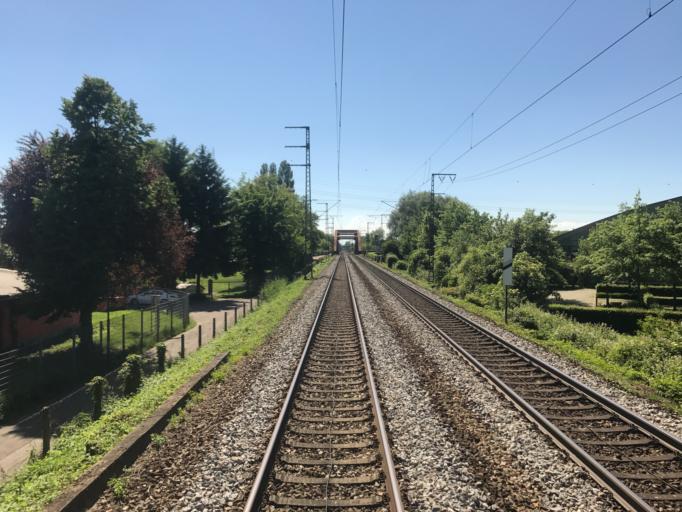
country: DE
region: Baden-Wuerttemberg
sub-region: Freiburg Region
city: Offenburg
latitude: 48.4630
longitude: 7.9408
